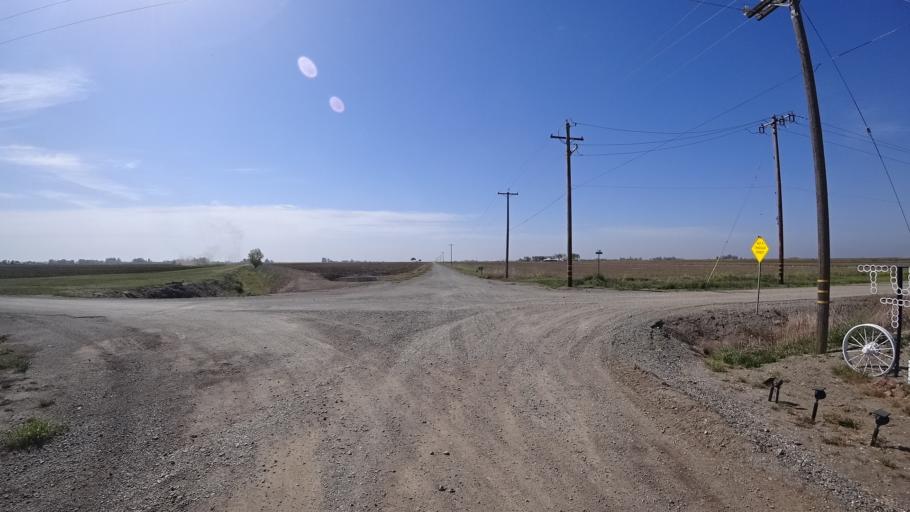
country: US
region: California
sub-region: Glenn County
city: Hamilton City
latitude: 39.6163
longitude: -122.0744
